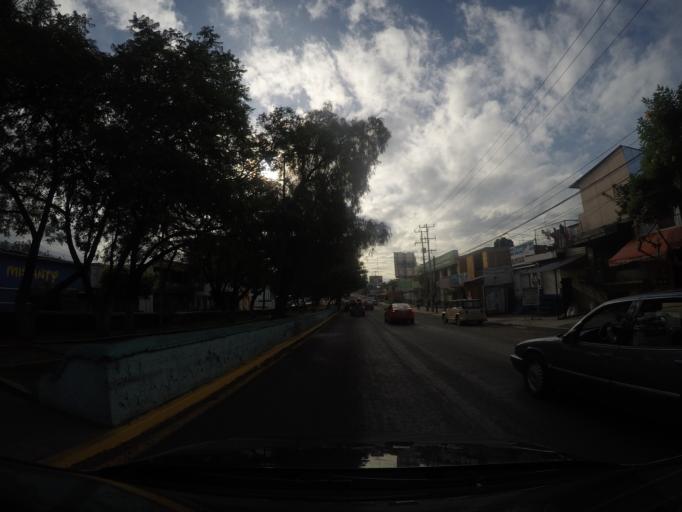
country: MX
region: Oaxaca
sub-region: Santa Cruz Amilpas
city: Santa Cruz Amilpas
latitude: 17.0693
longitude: -96.7011
